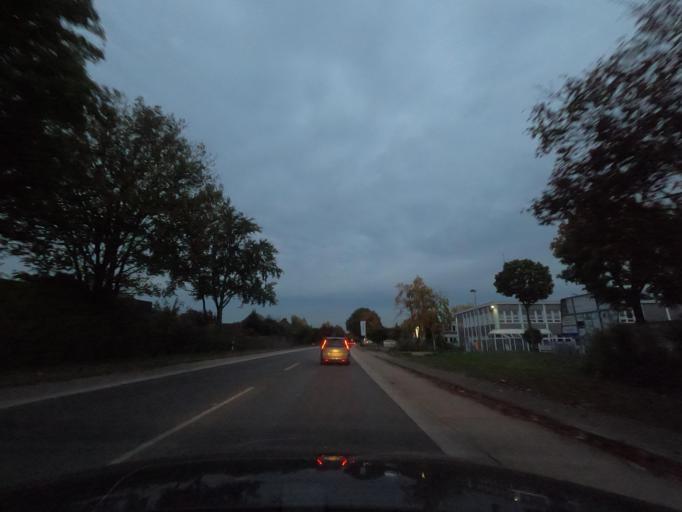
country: DE
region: North Rhine-Westphalia
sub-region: Regierungsbezirk Dusseldorf
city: Wesel
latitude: 51.6742
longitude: 6.6315
